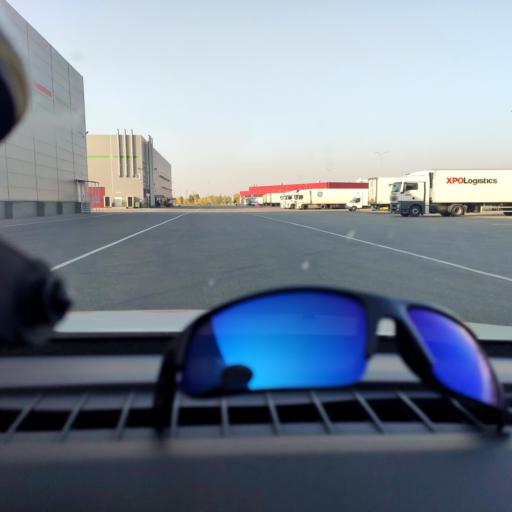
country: RU
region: Samara
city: Samara
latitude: 53.0953
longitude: 50.1341
